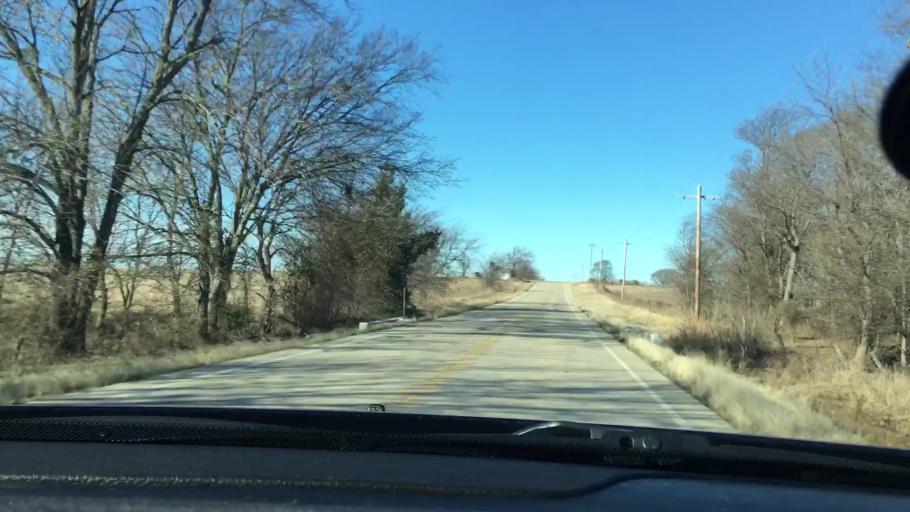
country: US
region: Oklahoma
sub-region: Marshall County
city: Madill
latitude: 34.1145
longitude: -96.6773
